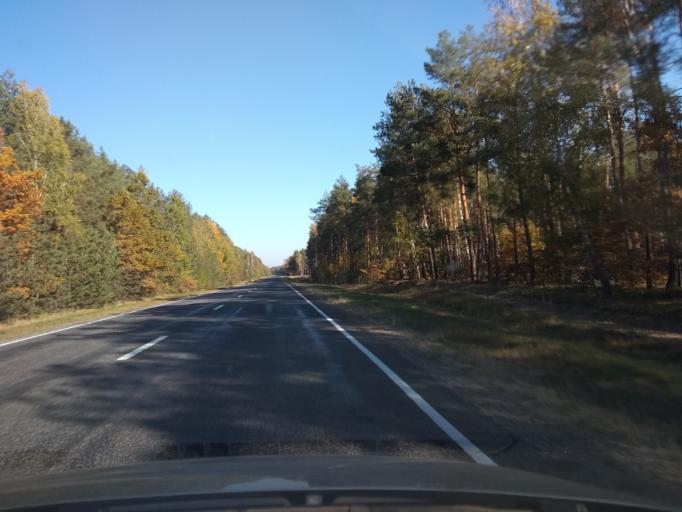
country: BY
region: Brest
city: Malaryta
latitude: 51.9549
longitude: 24.1867
